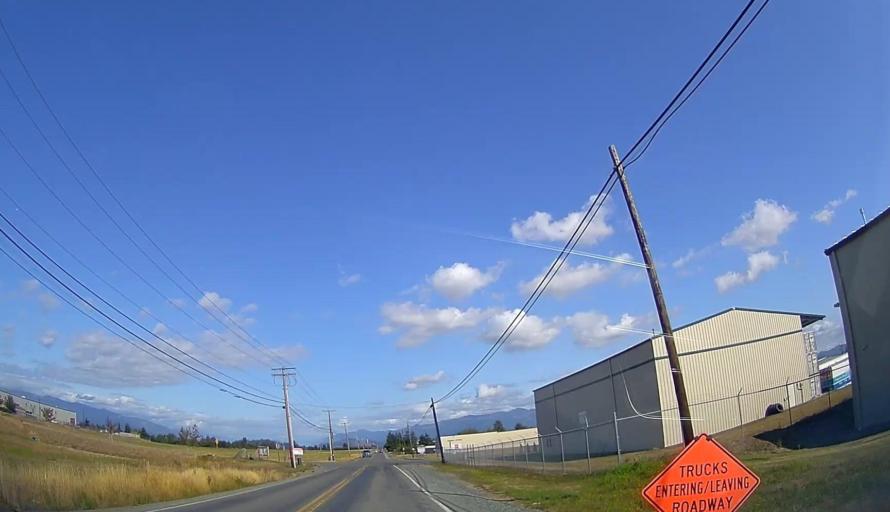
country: US
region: Washington
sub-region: Skagit County
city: Burlington
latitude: 48.4723
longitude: -122.4043
